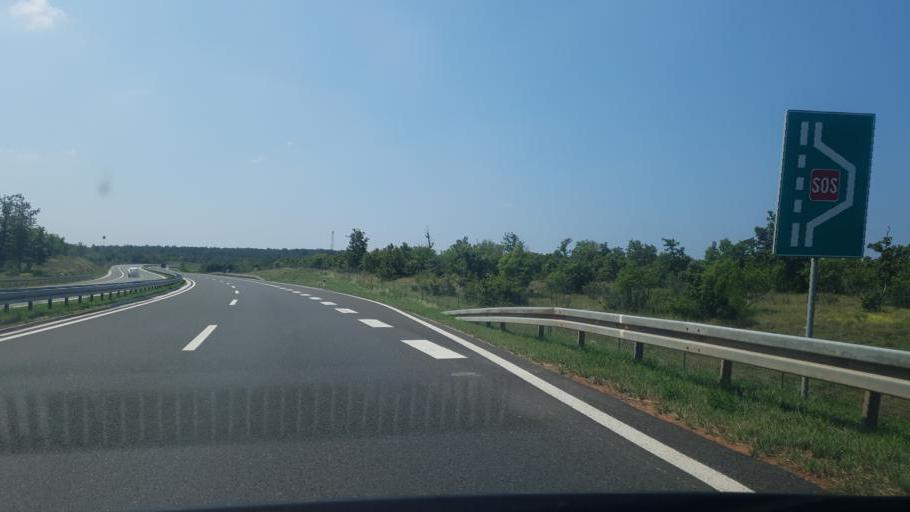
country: HR
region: Istarska
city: Vodnjan
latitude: 45.0642
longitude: 13.8389
